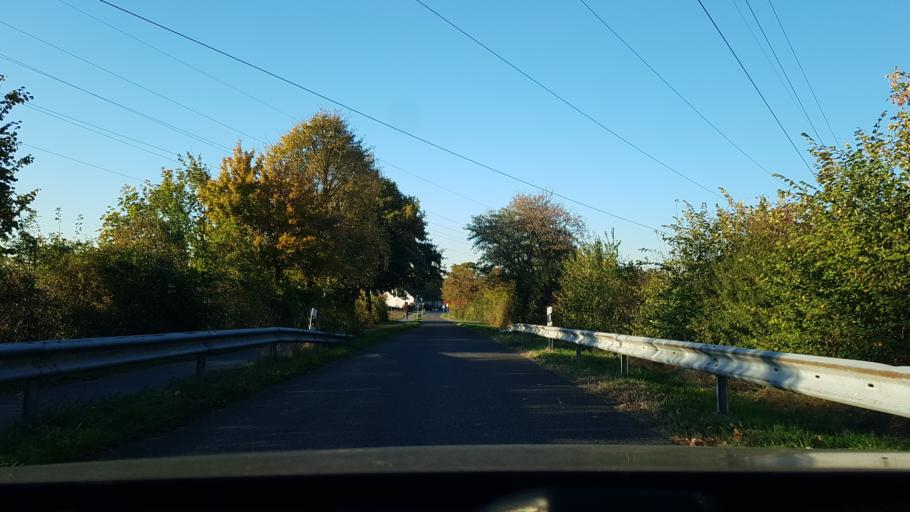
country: DE
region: North Rhine-Westphalia
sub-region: Regierungsbezirk Dusseldorf
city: Moers
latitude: 51.4346
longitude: 6.5816
